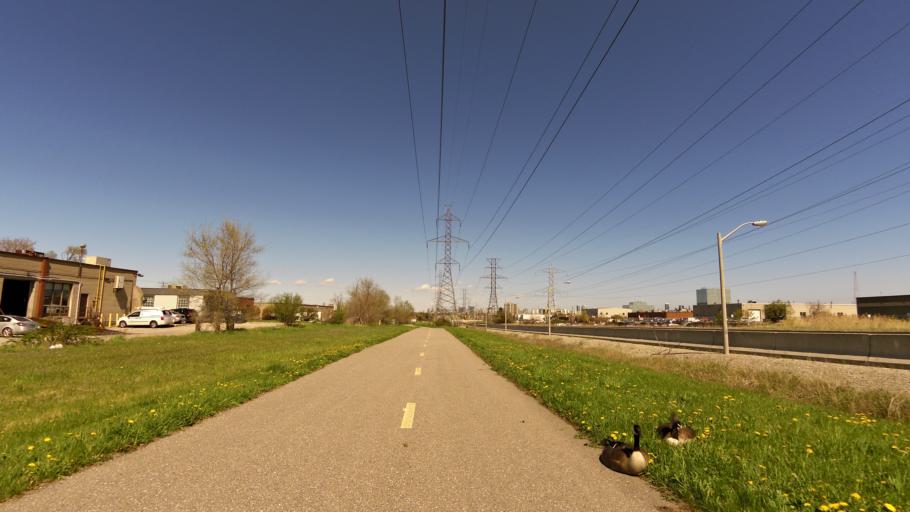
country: CA
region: Ontario
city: Concord
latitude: 43.7705
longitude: -79.4760
